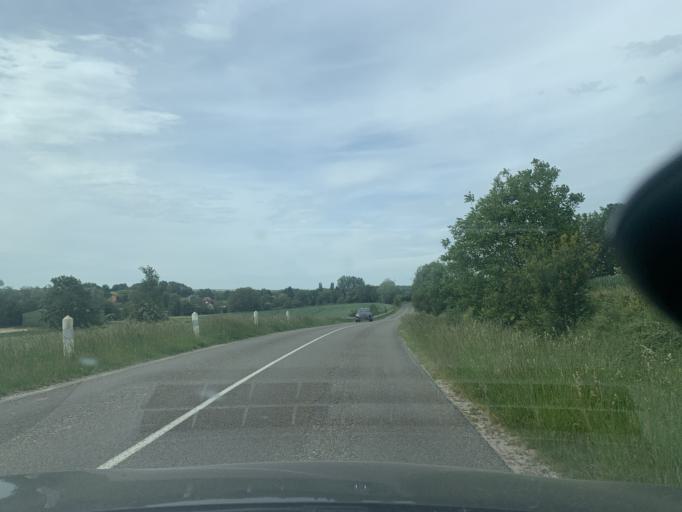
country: FR
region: Nord-Pas-de-Calais
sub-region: Departement du Nord
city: Marcoing
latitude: 50.1285
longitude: 3.1813
